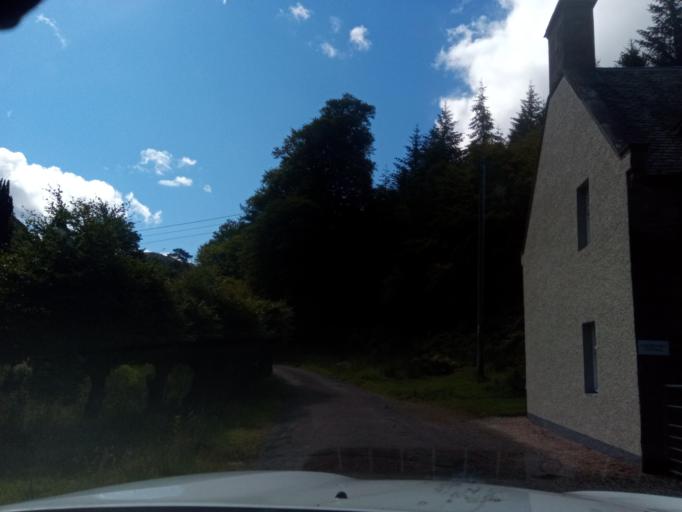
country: GB
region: Scotland
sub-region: Argyll and Bute
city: Isle Of Mull
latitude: 56.7795
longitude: -5.8252
